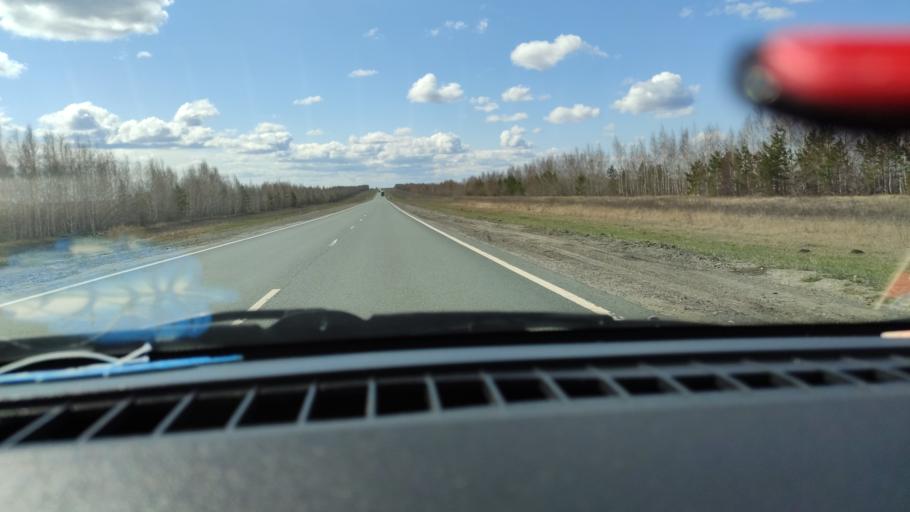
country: RU
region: Saratov
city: Dukhovnitskoye
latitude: 52.8240
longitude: 48.2359
